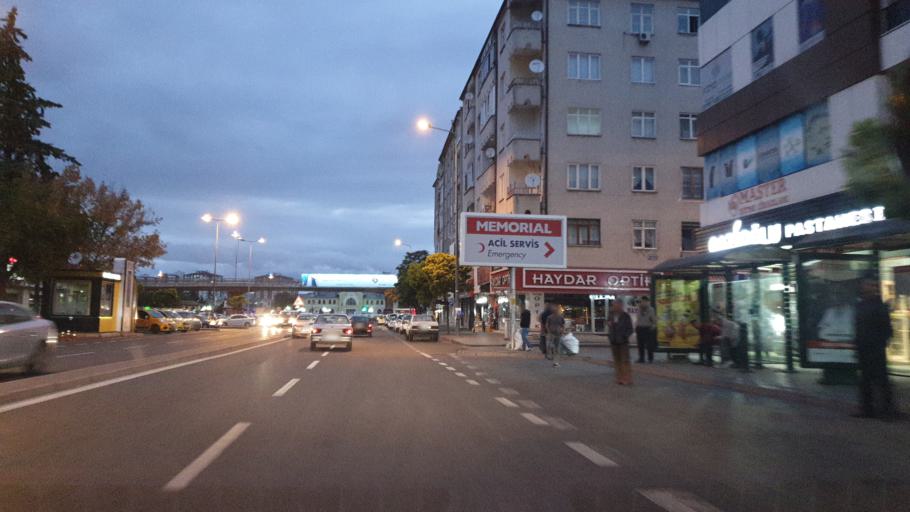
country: TR
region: Kayseri
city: Kayseri
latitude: 38.7279
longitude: 35.4793
